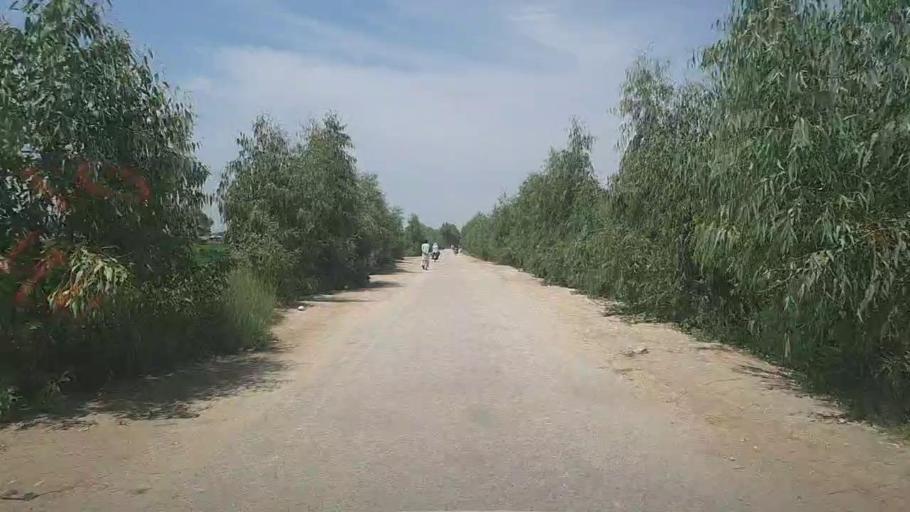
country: PK
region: Sindh
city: Kandhkot
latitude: 28.2936
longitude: 69.2376
